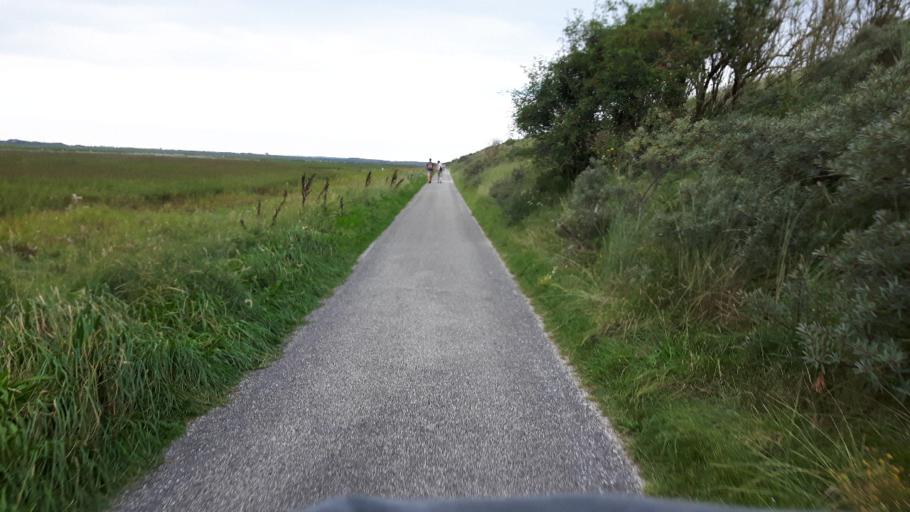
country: NL
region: Friesland
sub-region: Gemeente Dongeradeel
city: Holwerd
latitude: 53.4606
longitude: 5.8720
